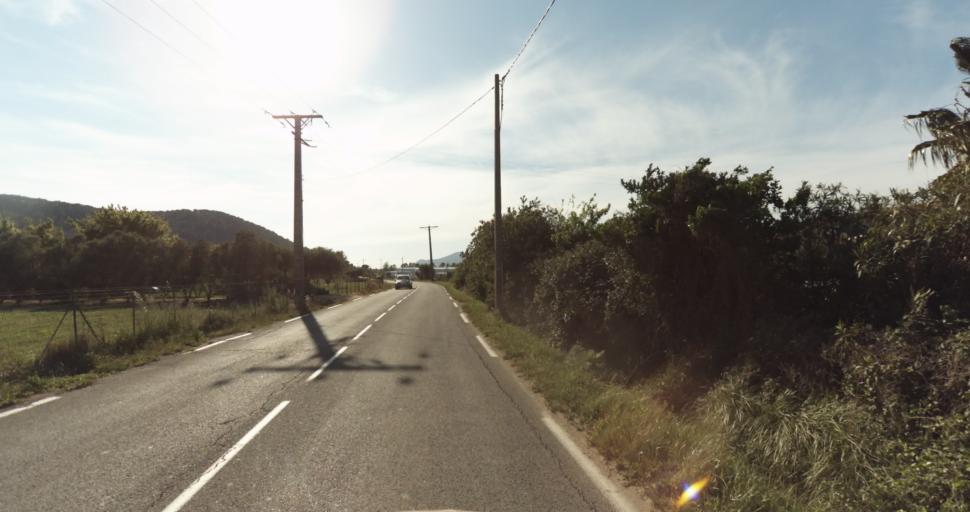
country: FR
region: Provence-Alpes-Cote d'Azur
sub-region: Departement du Var
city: Carqueiranne
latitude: 43.1171
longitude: 6.0882
